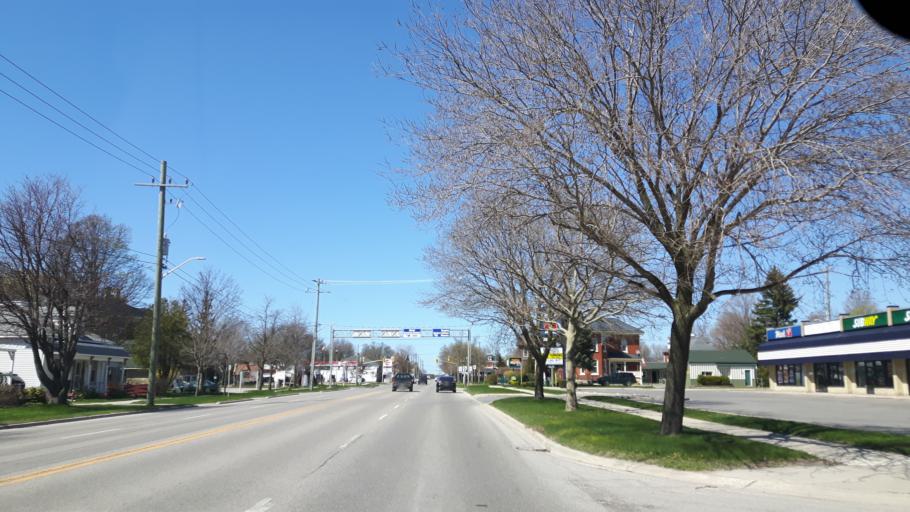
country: CA
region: Ontario
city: Goderich
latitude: 43.7439
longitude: -81.7077
